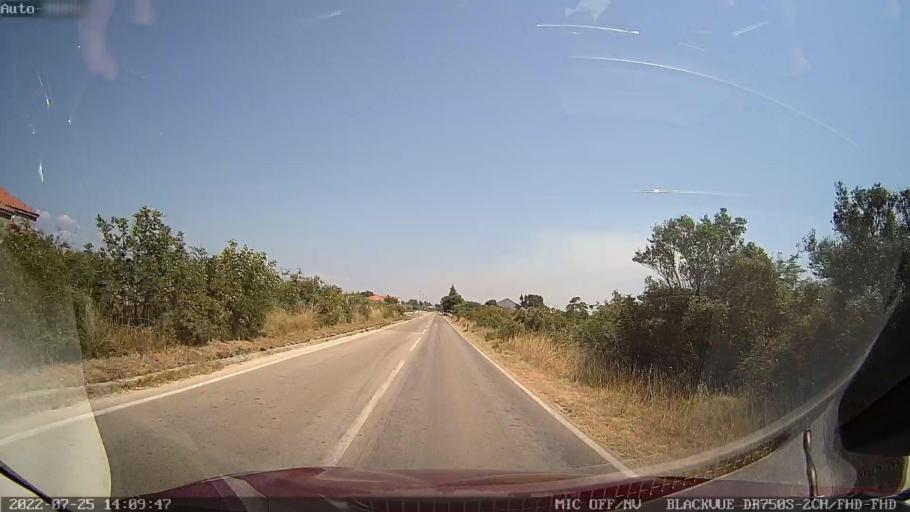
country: HR
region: Zadarska
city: Nin
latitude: 44.2268
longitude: 15.1997
